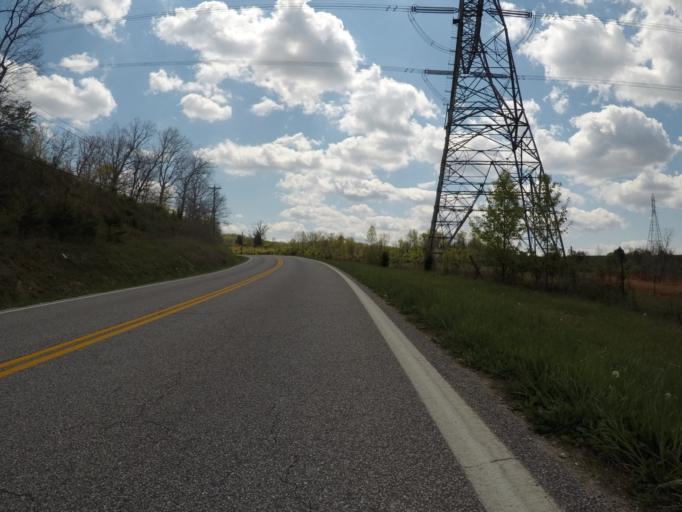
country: US
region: West Virginia
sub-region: Cabell County
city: Huntington
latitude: 38.4775
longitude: -82.3919
